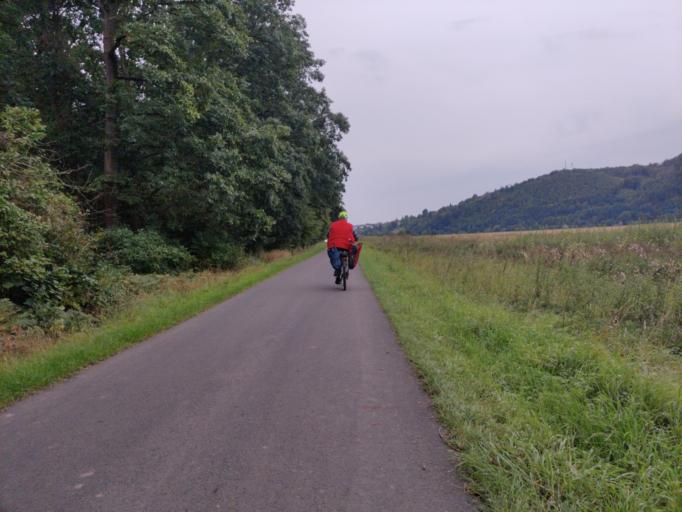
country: DE
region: Lower Saxony
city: Brevorde
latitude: 51.9055
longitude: 9.4256
